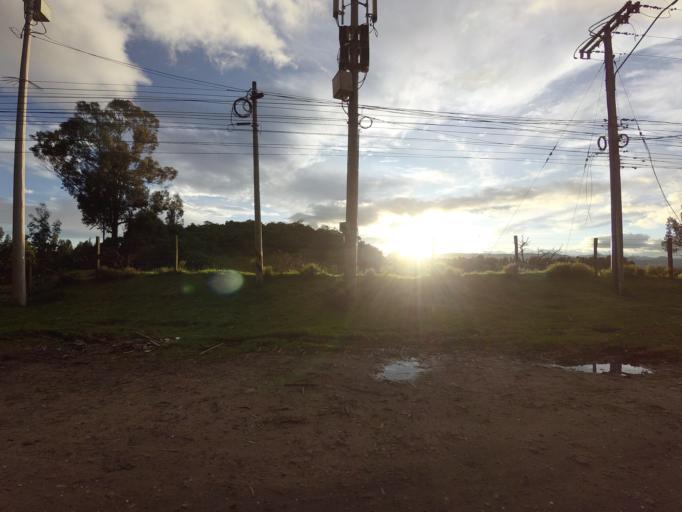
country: CO
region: Cundinamarca
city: Cota
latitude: 4.7846
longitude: -74.0282
